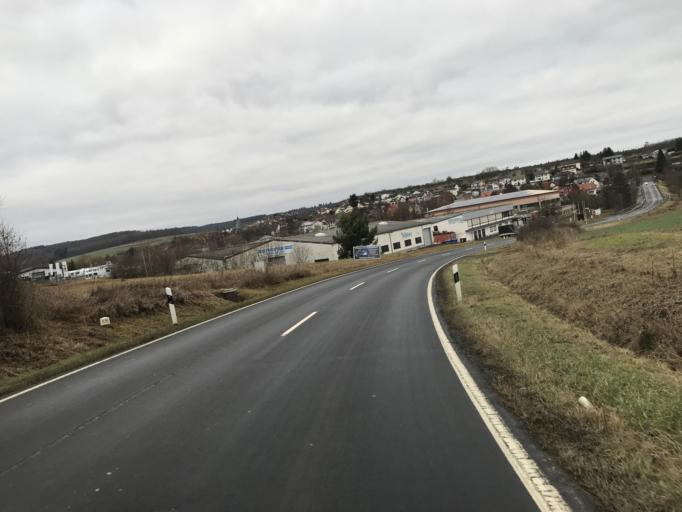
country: DE
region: Hesse
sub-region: Regierungsbezirk Giessen
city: Hoernsheim
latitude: 50.4580
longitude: 8.5975
